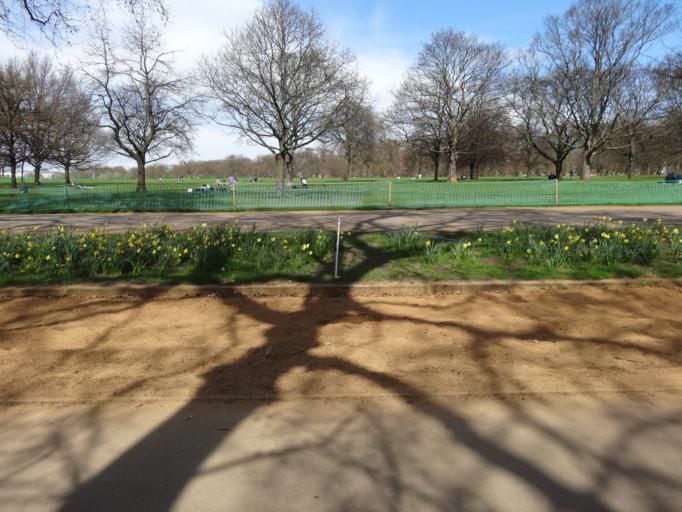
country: GB
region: England
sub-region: Greater London
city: Chelsea
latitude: 51.5050
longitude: -0.1583
